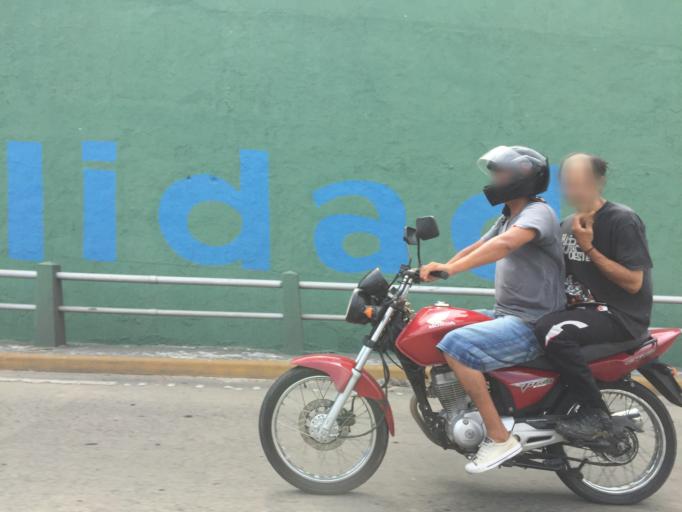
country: AR
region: Buenos Aires
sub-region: Partido de Avellaneda
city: Avellaneda
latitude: -34.6536
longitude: -58.3718
